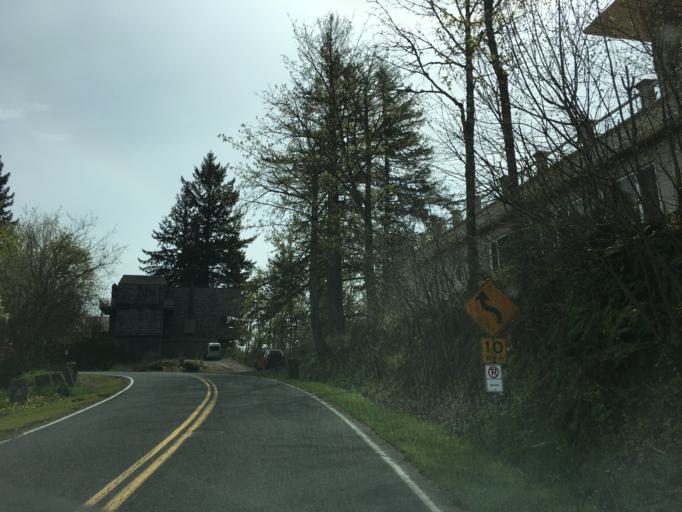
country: US
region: Oregon
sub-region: Multnomah County
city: Lents
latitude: 45.5428
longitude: -122.5670
